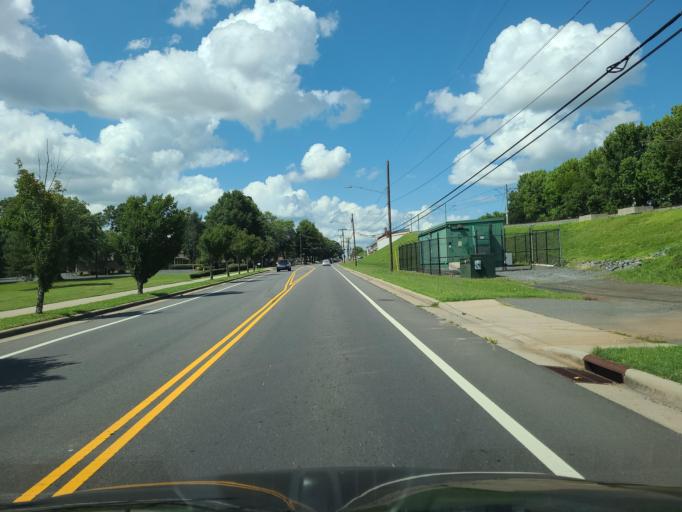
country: US
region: North Carolina
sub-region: Mecklenburg County
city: Pineville
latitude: 35.1500
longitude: -80.8784
